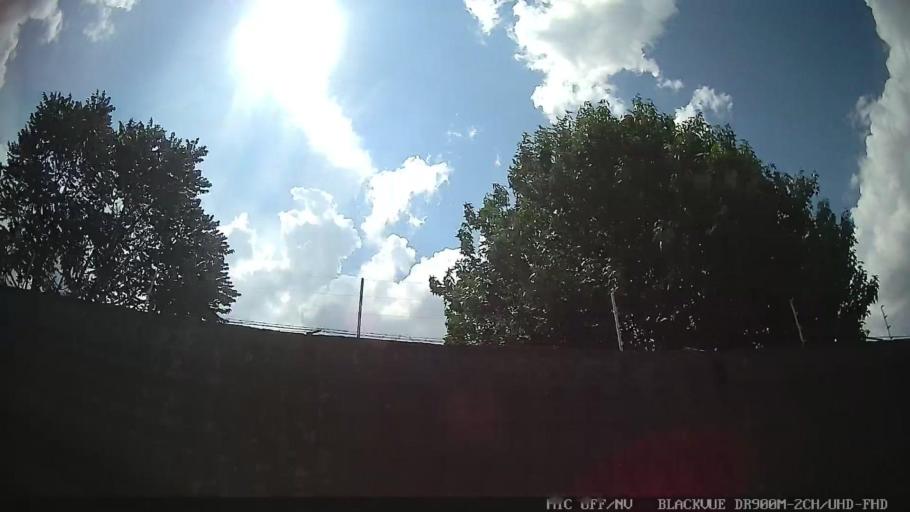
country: BR
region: Sao Paulo
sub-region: Braganca Paulista
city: Braganca Paulista
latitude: -22.9739
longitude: -46.5516
